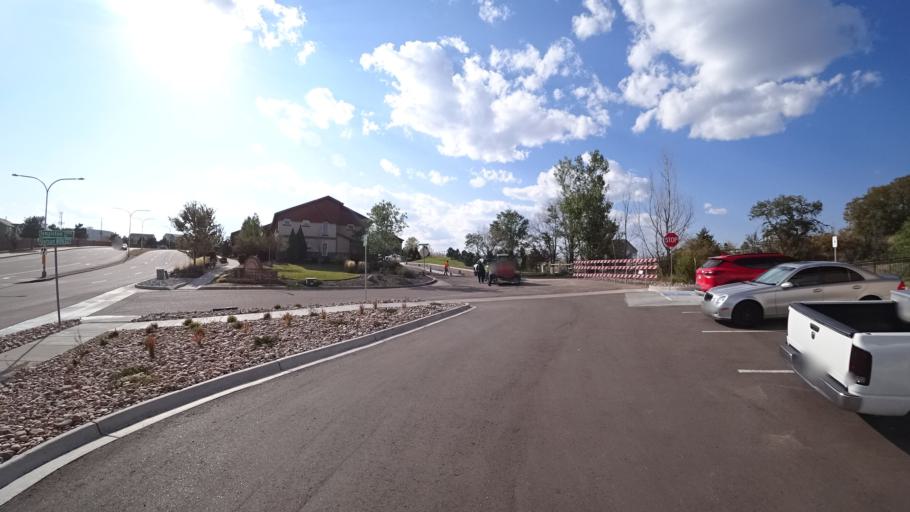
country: US
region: Colorado
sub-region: El Paso County
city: Cimarron Hills
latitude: 38.9125
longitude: -104.7259
